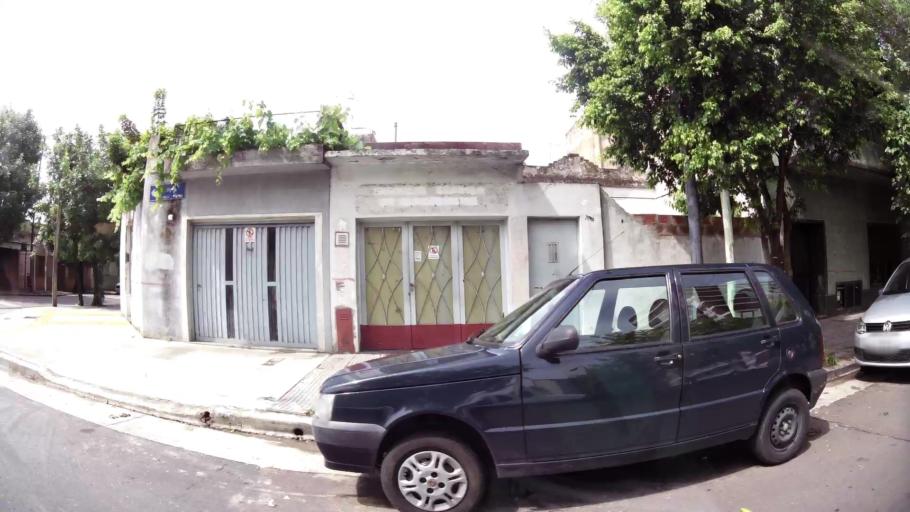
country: AR
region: Buenos Aires F.D.
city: Villa Santa Rita
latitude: -34.6244
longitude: -58.5216
